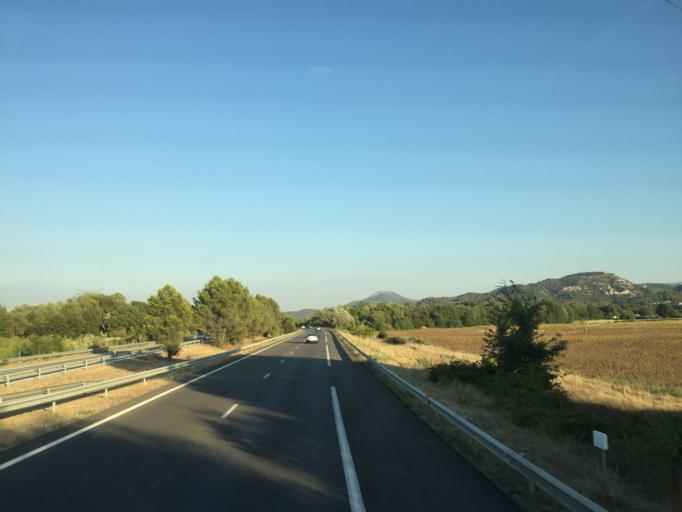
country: FR
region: Provence-Alpes-Cote d'Azur
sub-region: Departement des Bouches-du-Rhone
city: Meyrargues
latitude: 43.6599
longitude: 5.5165
